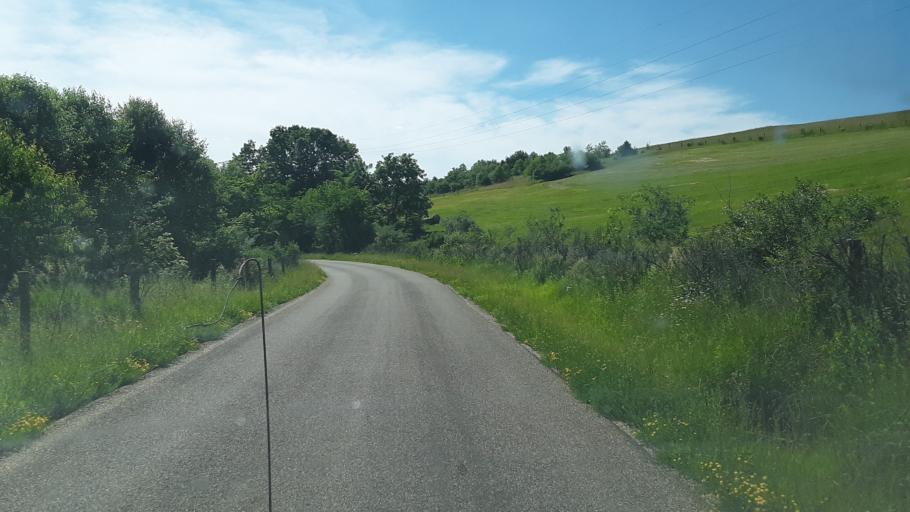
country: US
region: Ohio
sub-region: Coshocton County
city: West Lafayette
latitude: 40.2419
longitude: -81.7044
